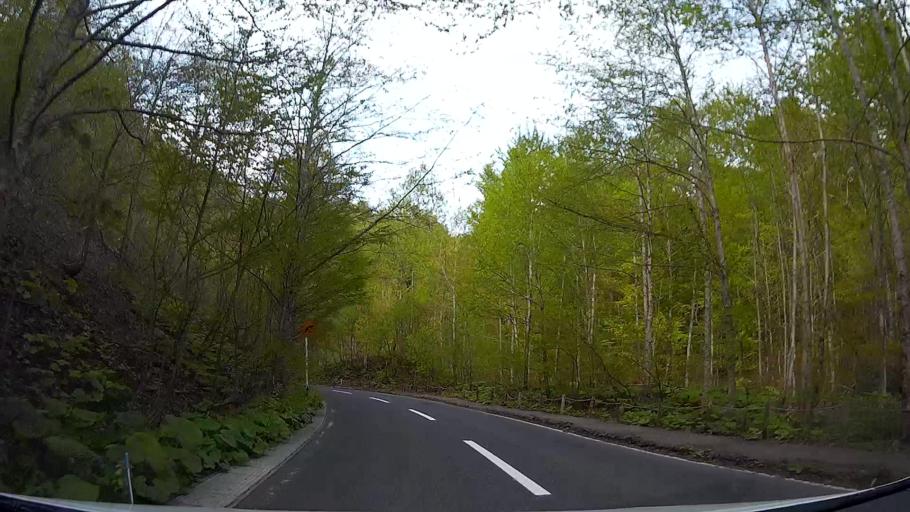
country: JP
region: Aomori
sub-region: Aomori Shi
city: Furudate
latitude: 40.5286
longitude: 140.9744
